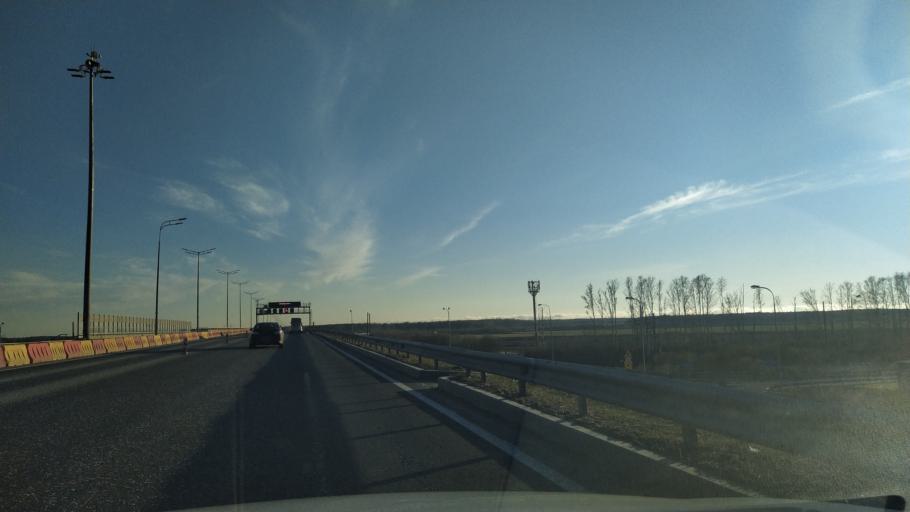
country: RU
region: St.-Petersburg
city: Pargolovo
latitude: 60.0930
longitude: 30.2472
